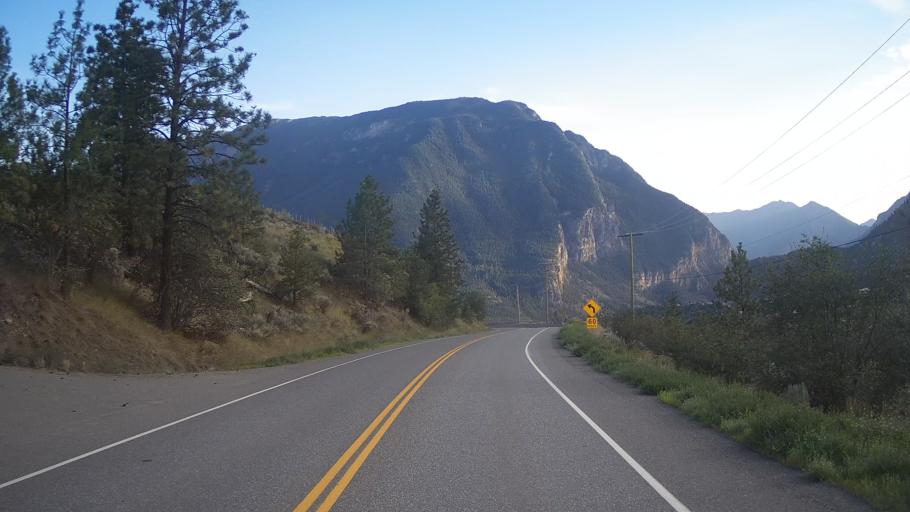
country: CA
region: British Columbia
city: Lillooet
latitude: 50.6949
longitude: -121.9194
